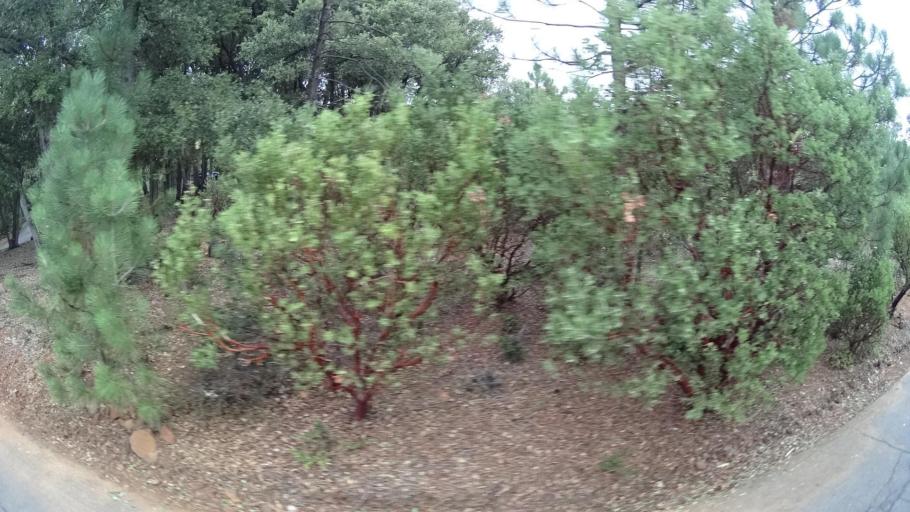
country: US
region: California
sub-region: San Diego County
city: Julian
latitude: 33.0426
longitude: -116.6293
